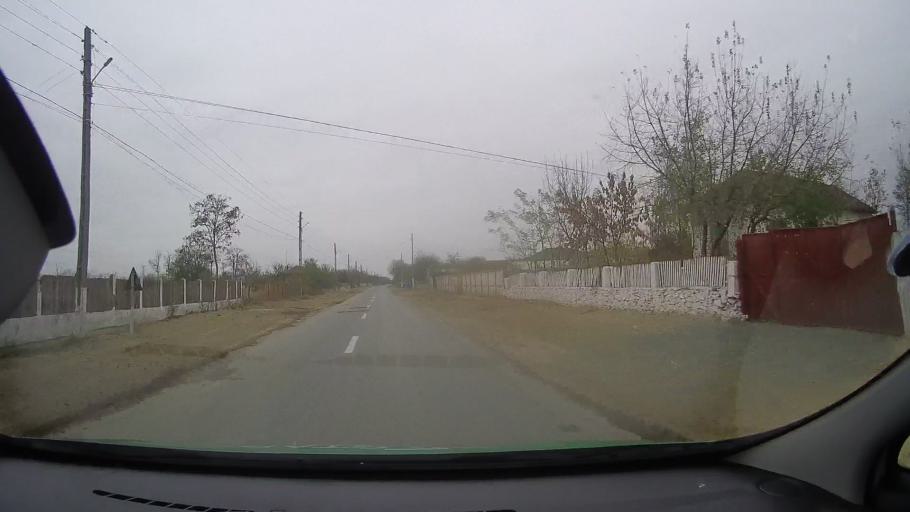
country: RO
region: Constanta
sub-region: Comuna Vulturu
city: Vulturu
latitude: 44.6411
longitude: 28.2740
